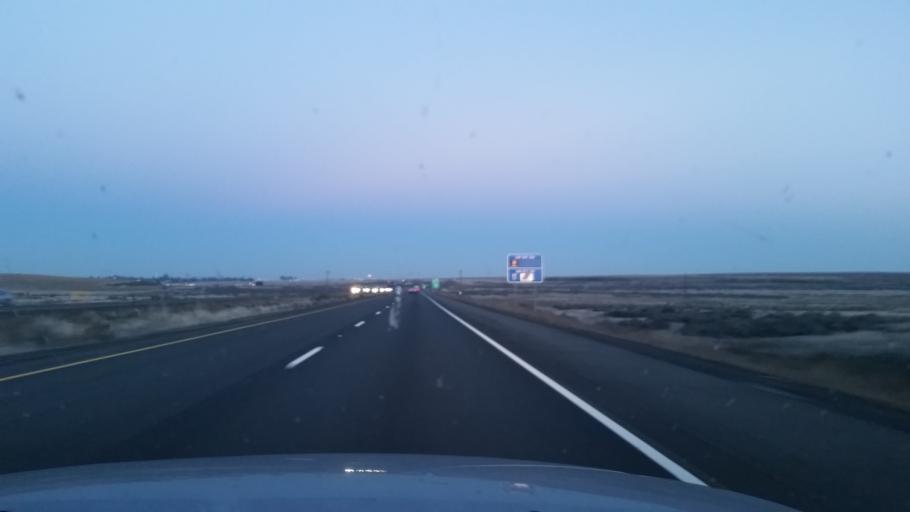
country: US
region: Washington
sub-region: Adams County
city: Ritzville
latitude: 47.1110
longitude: -118.4157
